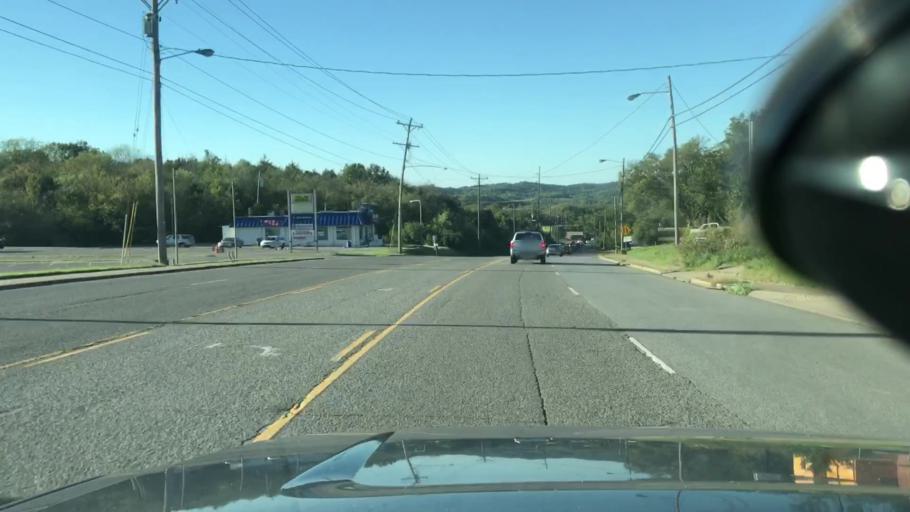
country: US
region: Tennessee
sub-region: Davidson County
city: Nashville
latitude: 36.1988
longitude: -86.8383
